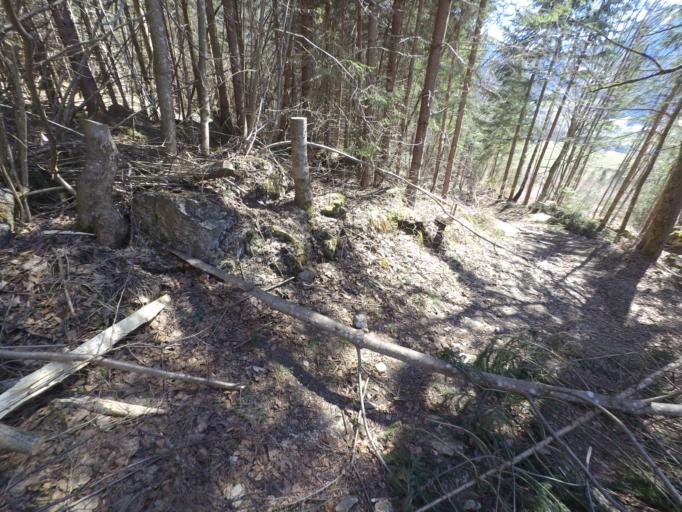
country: AT
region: Salzburg
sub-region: Politischer Bezirk Sankt Johann im Pongau
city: Sankt Veit im Pongau
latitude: 47.3335
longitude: 13.1635
